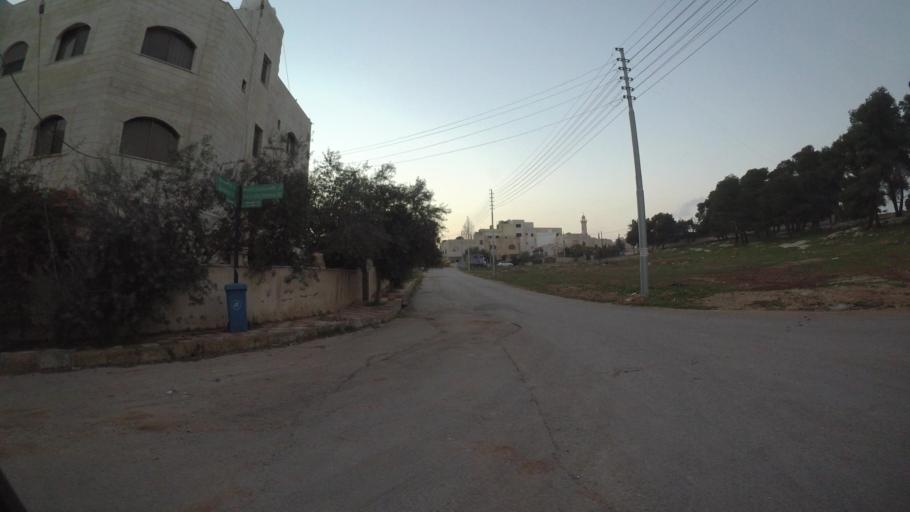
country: JO
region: Amman
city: Al Bunayyat ash Shamaliyah
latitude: 31.8907
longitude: 35.9234
